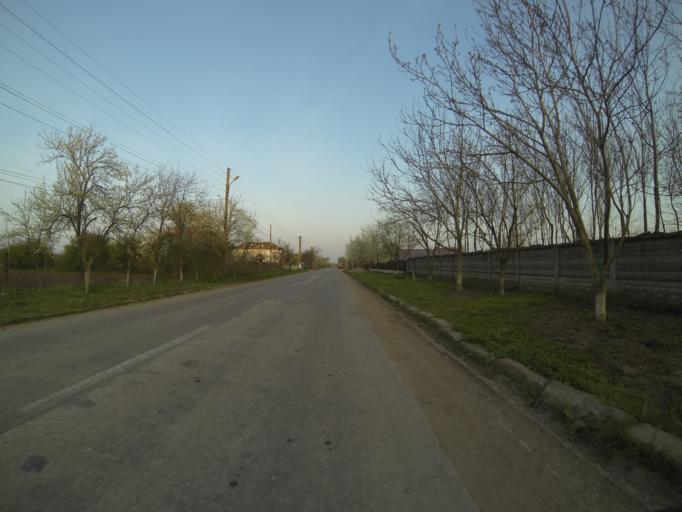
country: RO
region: Dolj
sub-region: Comuna Dranicu
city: Dranic
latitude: 44.0578
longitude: 23.8326
